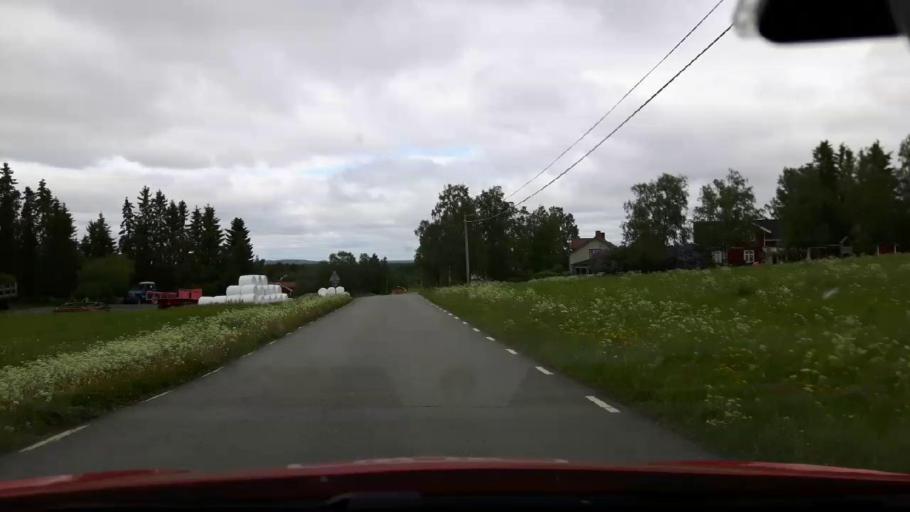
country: SE
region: Jaemtland
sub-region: Krokoms Kommun
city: Krokom
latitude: 63.2536
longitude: 14.5356
